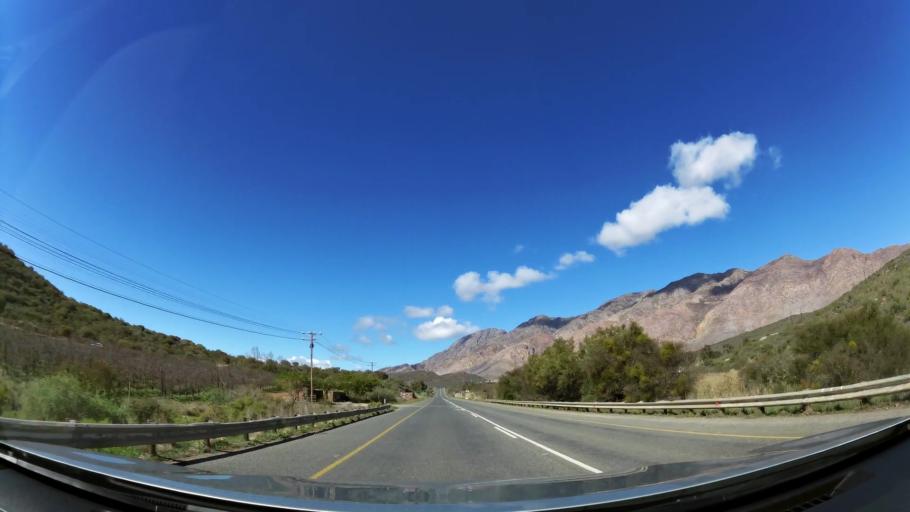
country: ZA
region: Western Cape
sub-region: Cape Winelands District Municipality
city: Ashton
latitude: -33.7901
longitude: 20.1362
